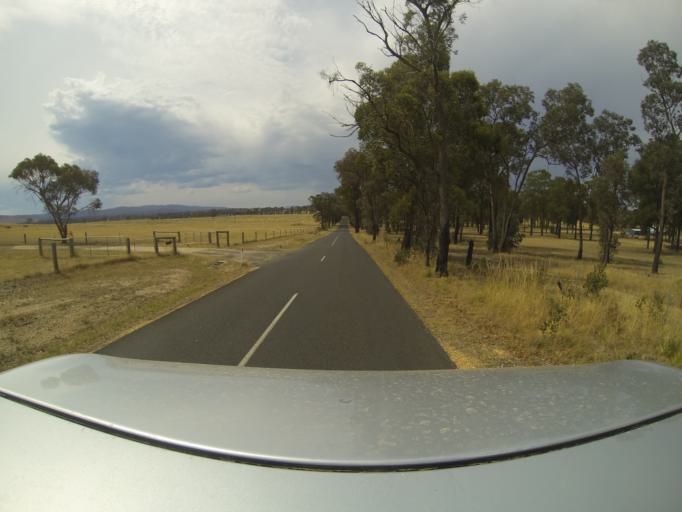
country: AU
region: Victoria
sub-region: Wellington
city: Heyfield
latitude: -37.9498
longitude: 146.6980
